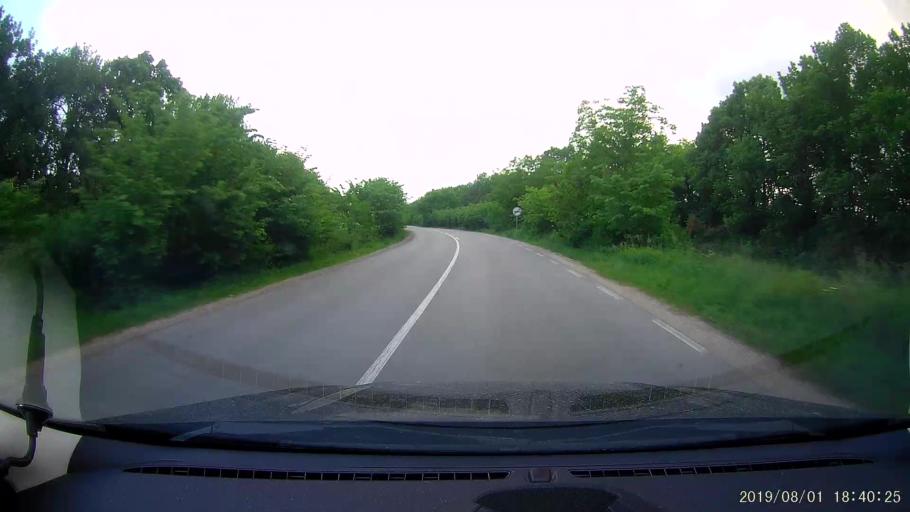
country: BG
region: Shumen
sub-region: Obshtina Khitrino
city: Gara Khitrino
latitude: 43.3676
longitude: 26.9193
